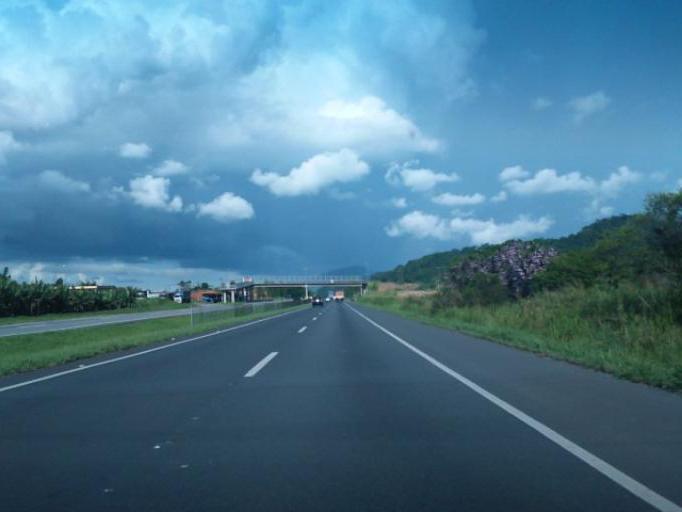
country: BR
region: Sao Paulo
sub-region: Juquia
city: Juquia
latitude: -24.3265
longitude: -47.5635
